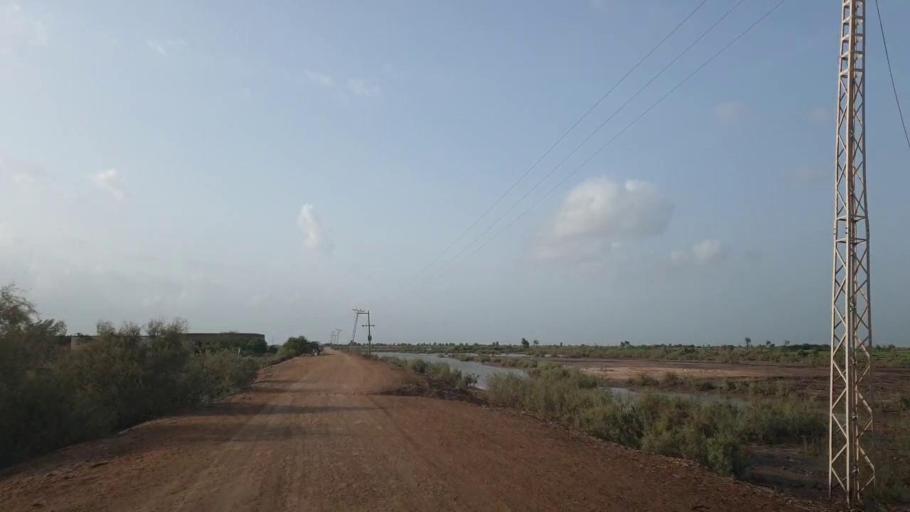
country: PK
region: Sindh
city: Tando Bago
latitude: 24.6508
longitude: 69.1119
